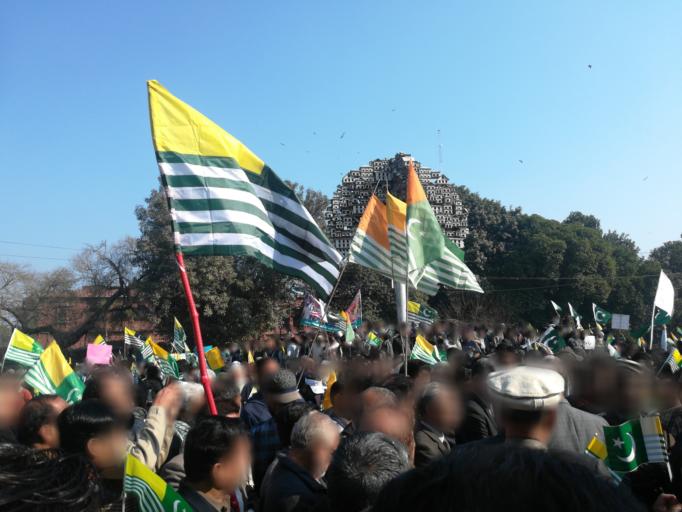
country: PK
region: Punjab
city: Lahore
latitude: 31.5689
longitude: 74.3069
